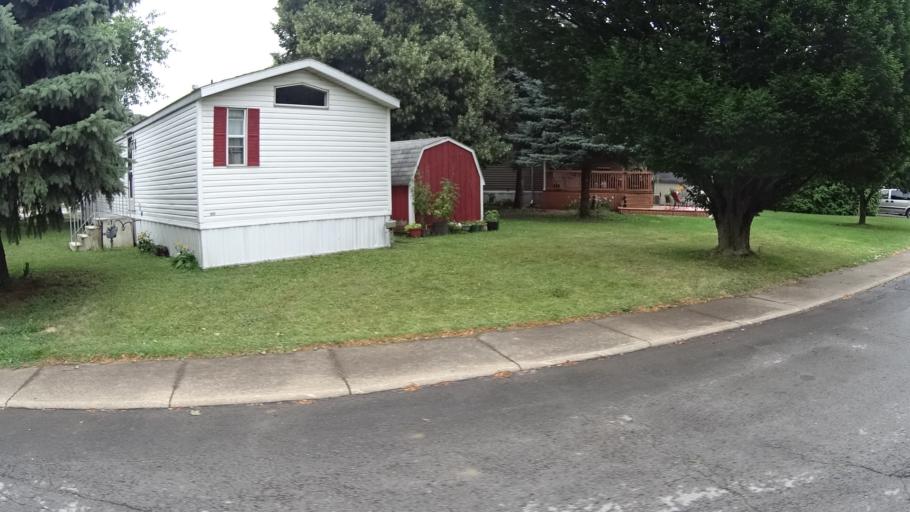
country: US
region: Ohio
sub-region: Erie County
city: Sandusky
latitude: 41.4394
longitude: -82.6661
